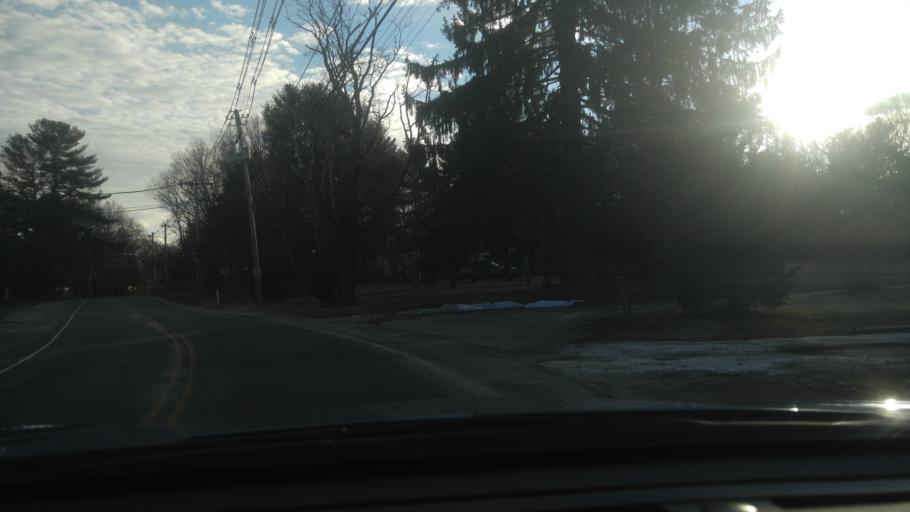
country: US
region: Rhode Island
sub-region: Kent County
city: East Greenwich
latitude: 41.6091
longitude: -71.4785
